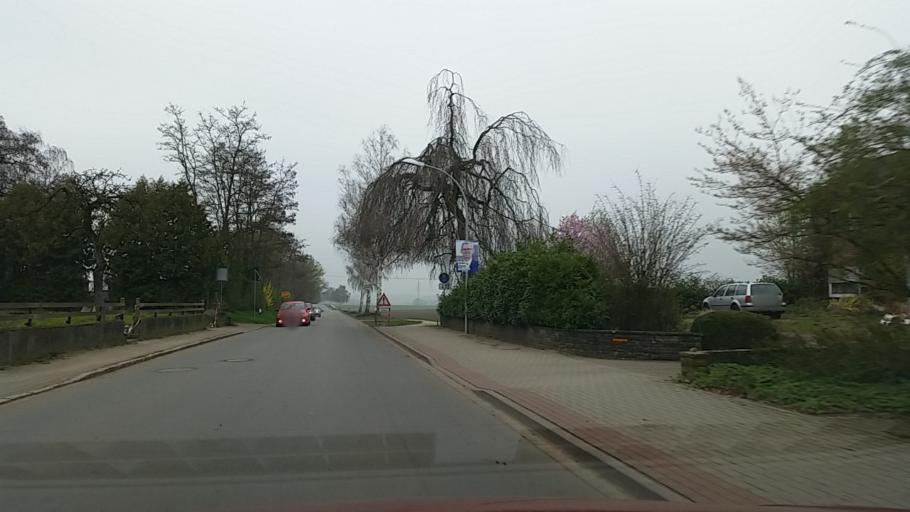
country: DE
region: Lower Saxony
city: Suderburg
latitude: 52.9367
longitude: 10.4854
